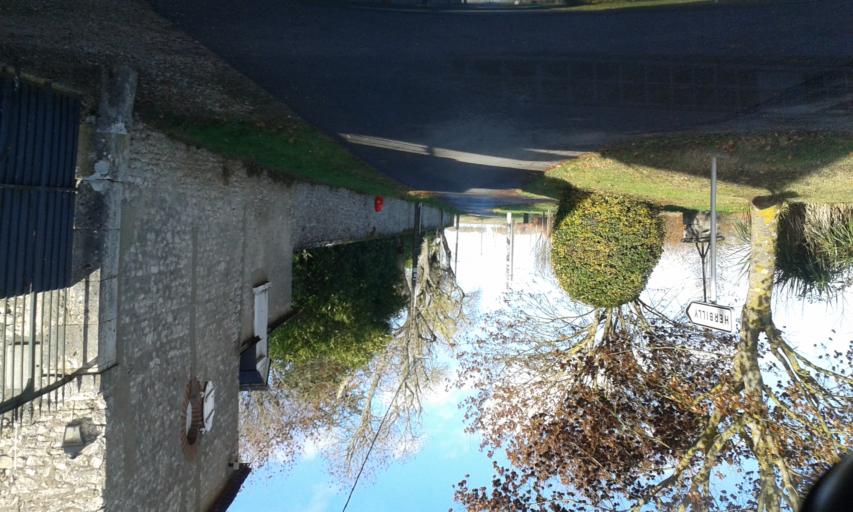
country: FR
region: Centre
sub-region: Departement du Loir-et-Cher
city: Mer
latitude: 47.6997
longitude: 1.5219
